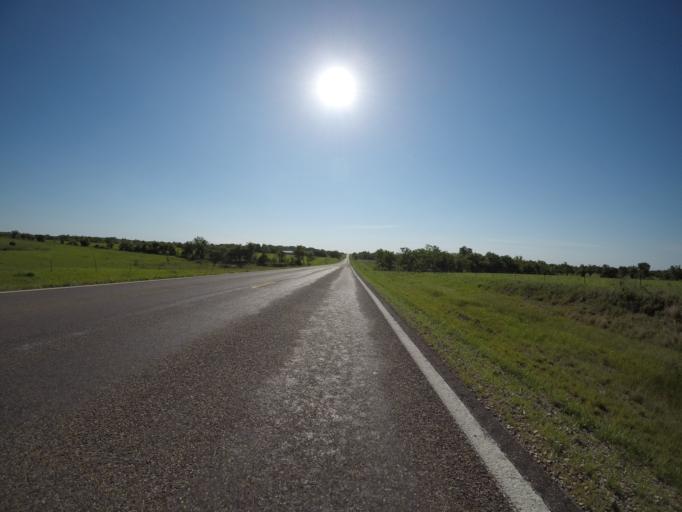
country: US
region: Kansas
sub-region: Lyon County
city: Emporia
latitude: 38.6589
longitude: -96.2312
